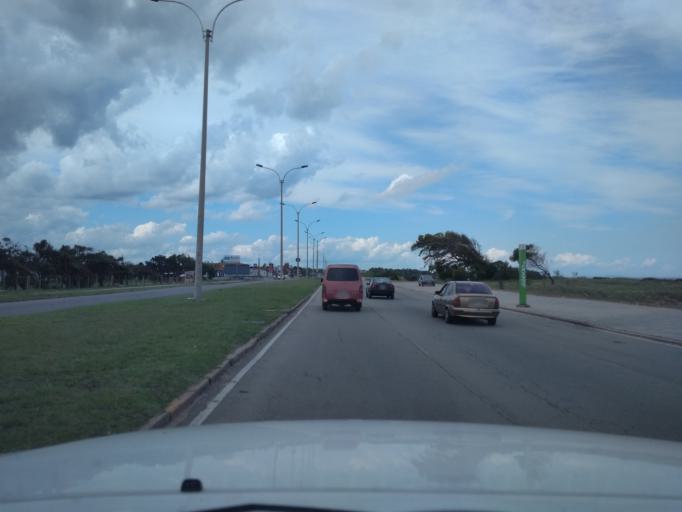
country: UY
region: Canelones
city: Barra de Carrasco
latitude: -34.8805
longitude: -56.0323
